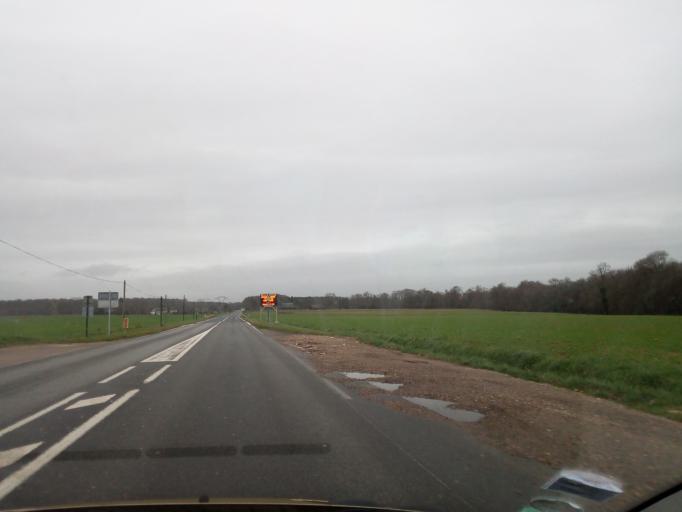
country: FR
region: Haute-Normandie
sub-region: Departement de l'Eure
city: Hauville
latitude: 49.4040
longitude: 0.7973
